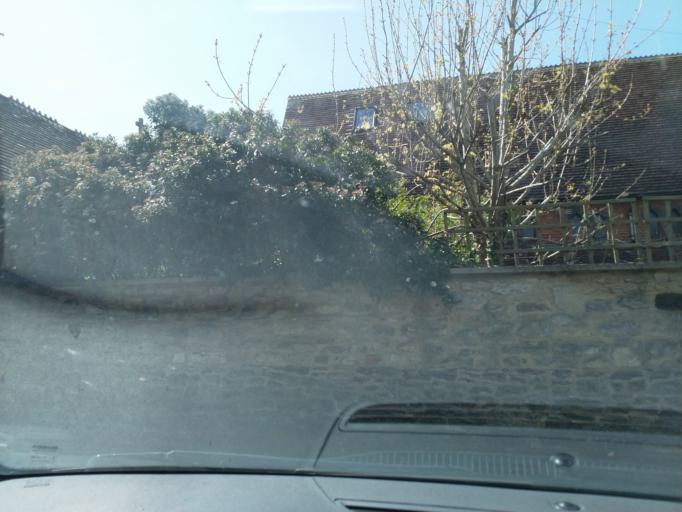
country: GB
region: England
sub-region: Oxfordshire
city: Cowley
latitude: 51.7381
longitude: -1.2100
